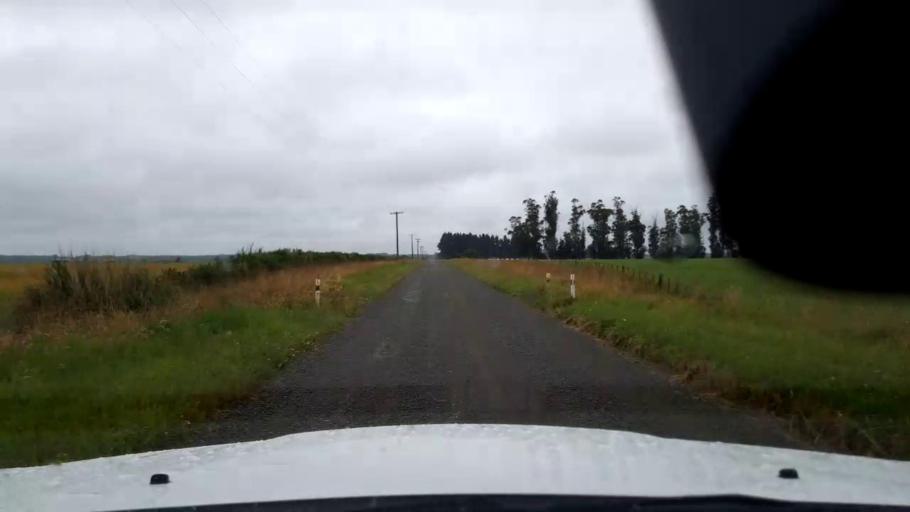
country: NZ
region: Canterbury
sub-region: Timaru District
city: Pleasant Point
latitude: -44.2358
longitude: 171.2021
